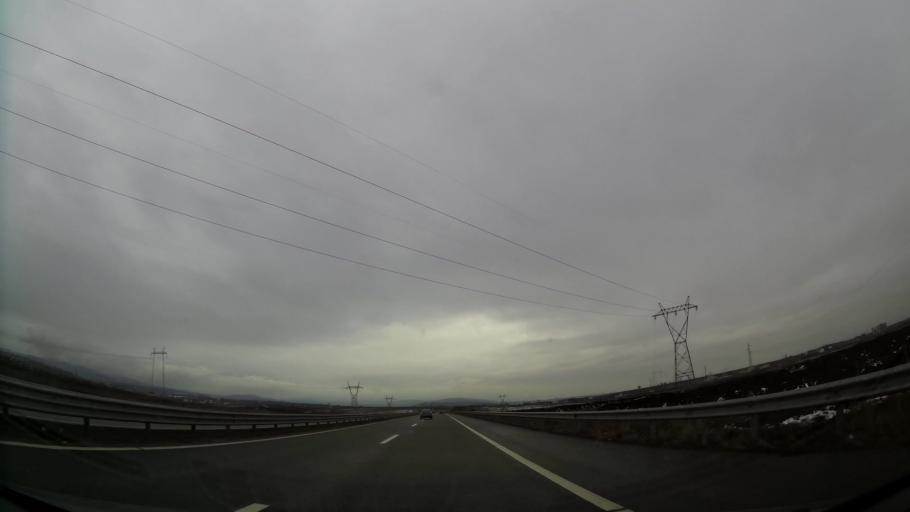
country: XK
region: Pristina
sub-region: Lipjan
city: Lipljan
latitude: 42.5145
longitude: 21.1754
